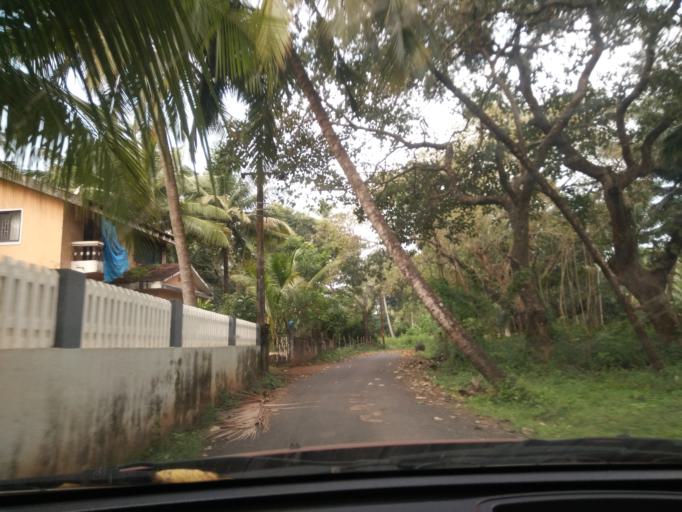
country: IN
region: Goa
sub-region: South Goa
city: Varca
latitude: 15.2274
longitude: 73.9522
